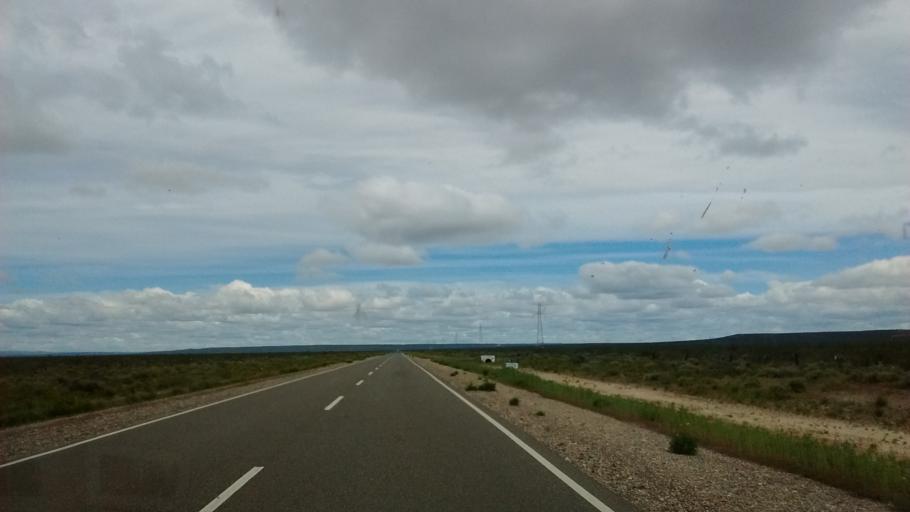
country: AR
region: Neuquen
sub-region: Departamento de Picun Leufu
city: Picun Leufu
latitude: -39.6714
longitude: -69.4448
